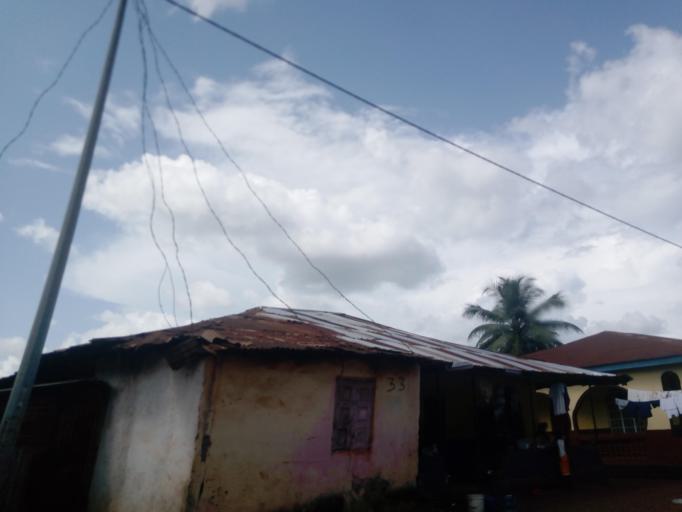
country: SL
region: Northern Province
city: Makeni
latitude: 8.8912
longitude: -12.0376
